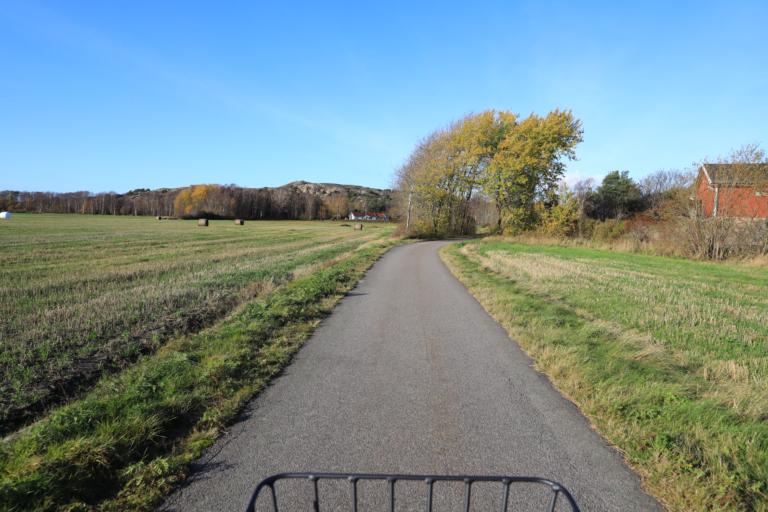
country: SE
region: Halland
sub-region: Varbergs Kommun
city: Varberg
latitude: 57.1540
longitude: 12.2417
